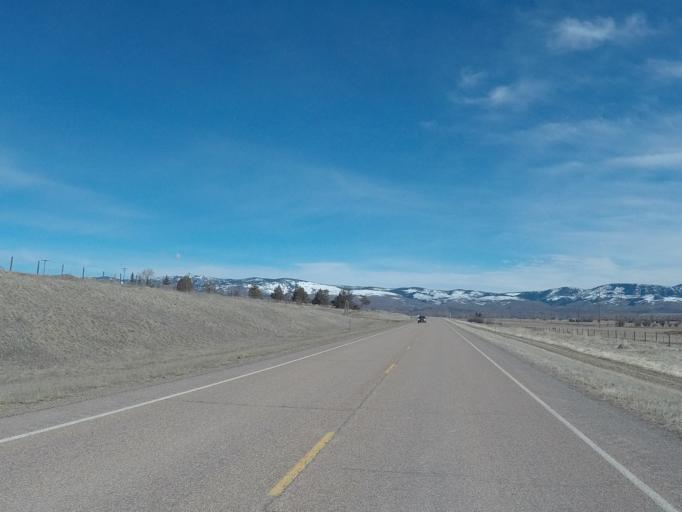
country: US
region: Montana
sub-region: Granite County
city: Philipsburg
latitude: 46.5975
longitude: -113.1897
